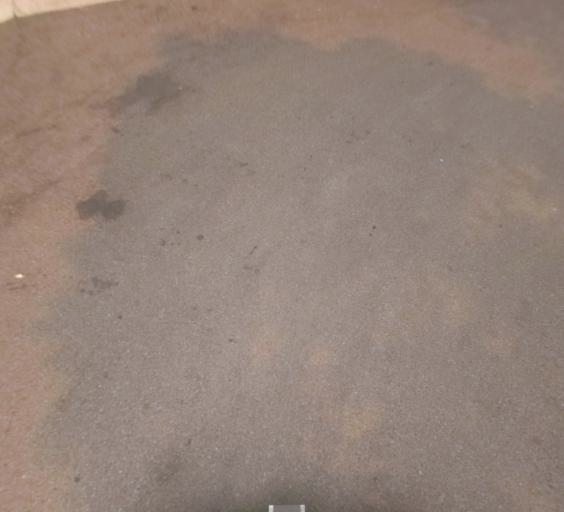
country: US
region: California
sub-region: Madera County
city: Oakhurst
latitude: 37.3231
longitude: -119.5669
